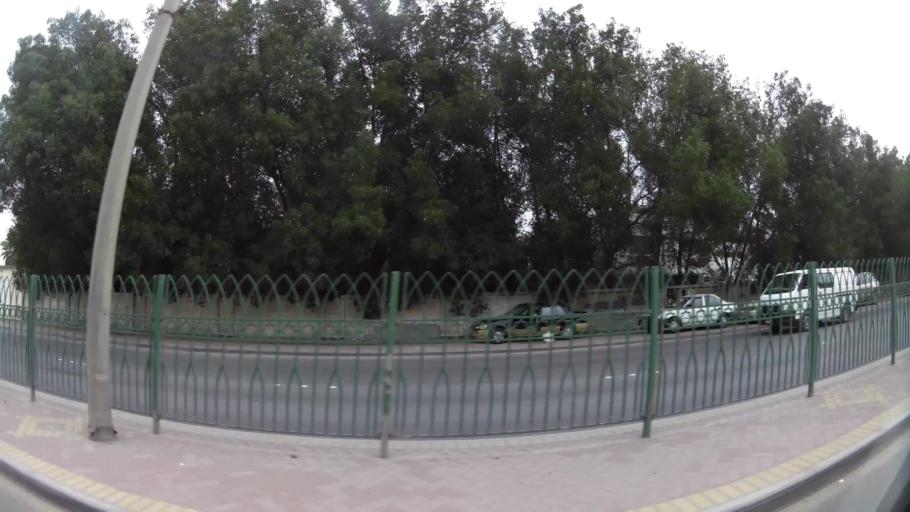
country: BH
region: Manama
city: Jidd Hafs
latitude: 26.2048
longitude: 50.5343
